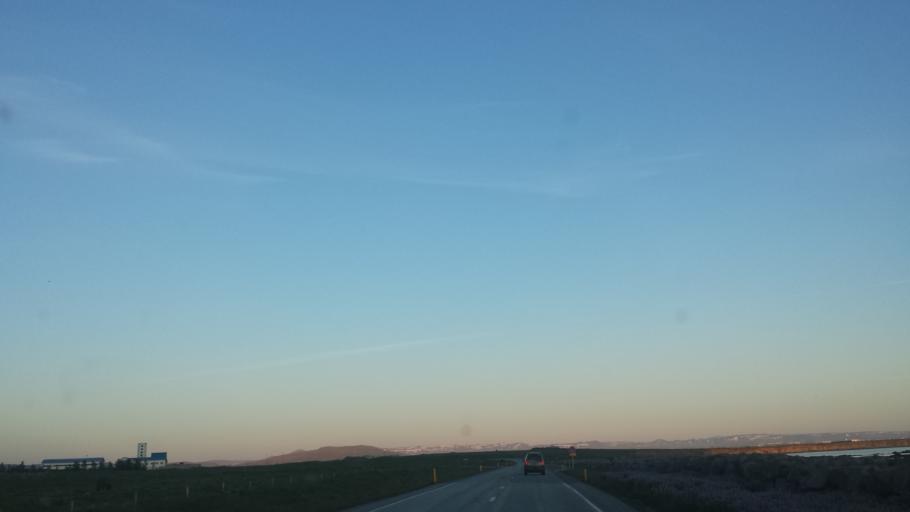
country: IS
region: Capital Region
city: Reykjavik
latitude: 64.2312
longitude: -21.8168
